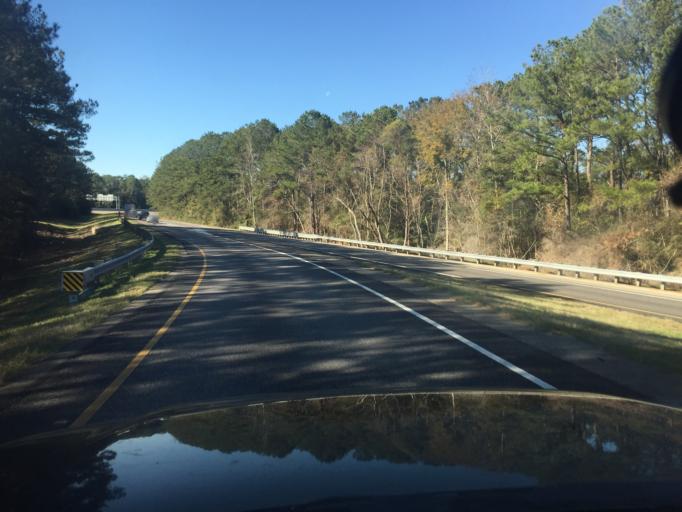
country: US
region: Louisiana
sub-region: Saint Tammany Parish
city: Slidell
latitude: 30.3087
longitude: -89.7425
